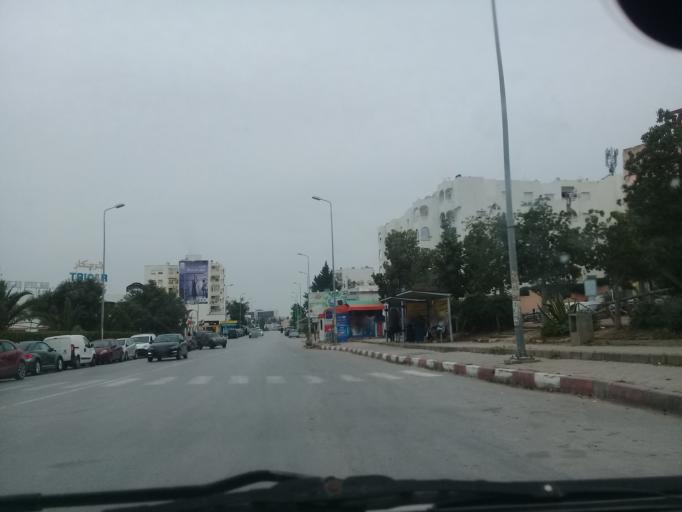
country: TN
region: Tunis
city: Tunis
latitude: 36.8457
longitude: 10.1533
